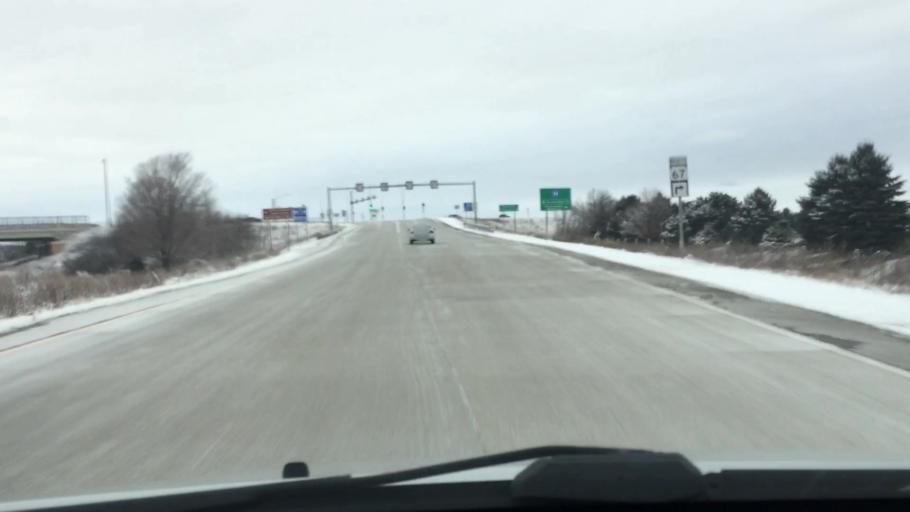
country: US
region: Wisconsin
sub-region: Waukesha County
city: Oconomowoc
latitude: 43.0689
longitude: -88.4684
